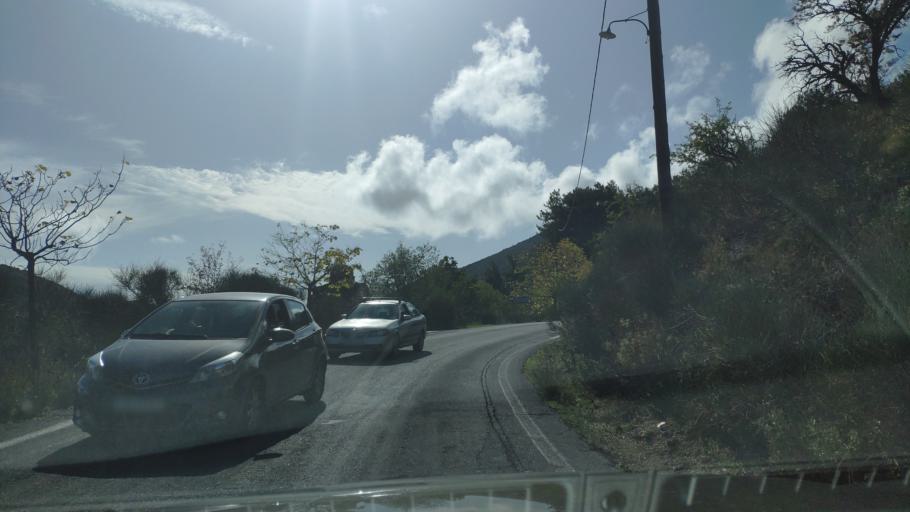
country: GR
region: Peloponnese
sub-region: Nomos Arkadias
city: Dimitsana
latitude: 37.5917
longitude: 22.0279
